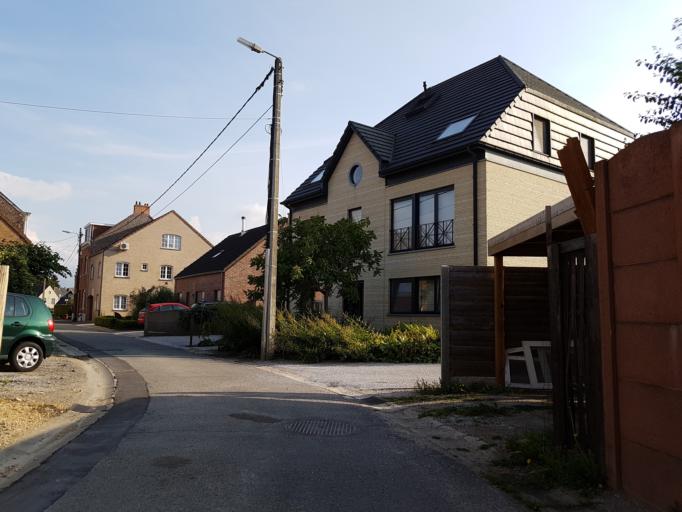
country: BE
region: Flanders
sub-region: Provincie Vlaams-Brabant
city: Zaventem
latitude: 50.9157
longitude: 4.4769
